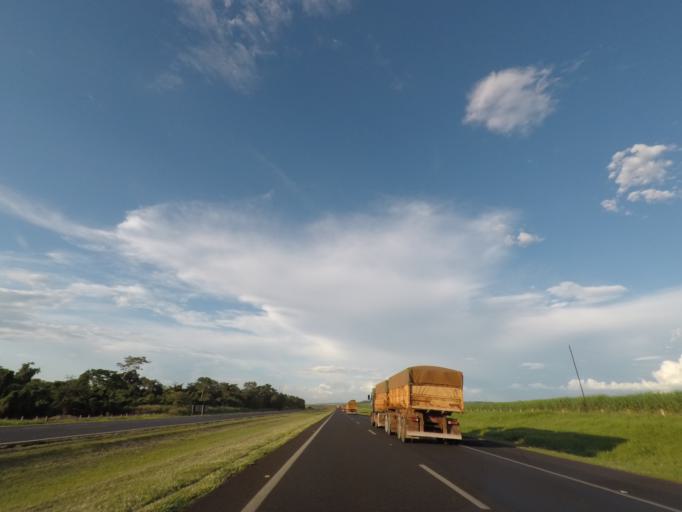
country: BR
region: Sao Paulo
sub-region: Ituverava
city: Ituverava
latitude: -20.3060
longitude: -47.8004
